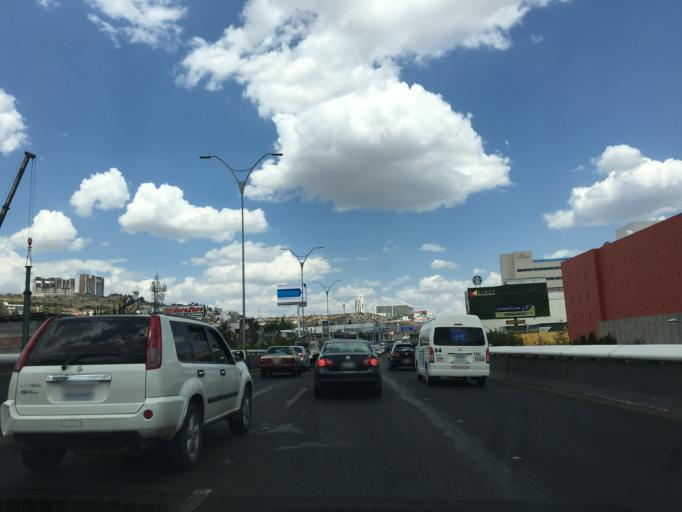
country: MX
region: Queretaro
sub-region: Queretaro
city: Santiago de Queretaro
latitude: 20.6159
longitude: -100.3893
